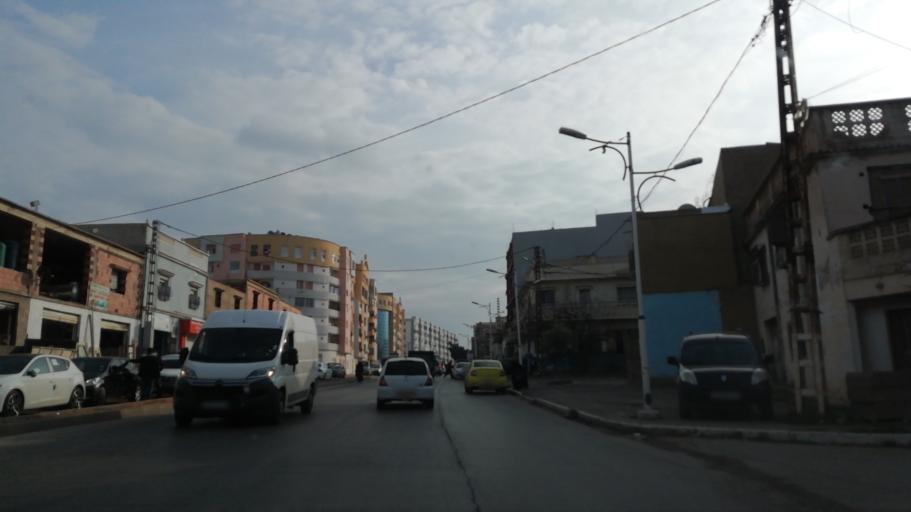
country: DZ
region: Mostaganem
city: Mostaganem
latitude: 35.8951
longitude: 0.0758
